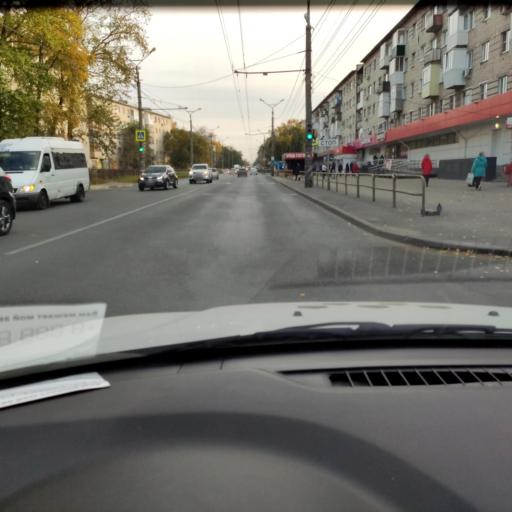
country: RU
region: Samara
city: Tol'yatti
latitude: 53.5271
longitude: 49.4132
